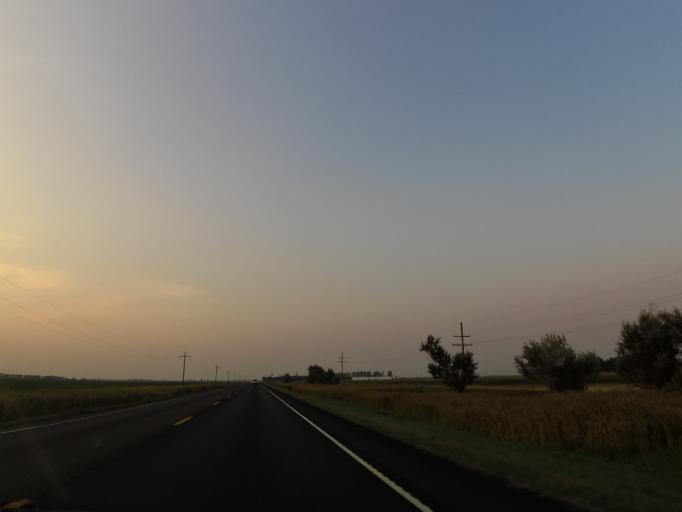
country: US
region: North Dakota
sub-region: Walsh County
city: Park River
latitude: 48.2183
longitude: -97.6226
